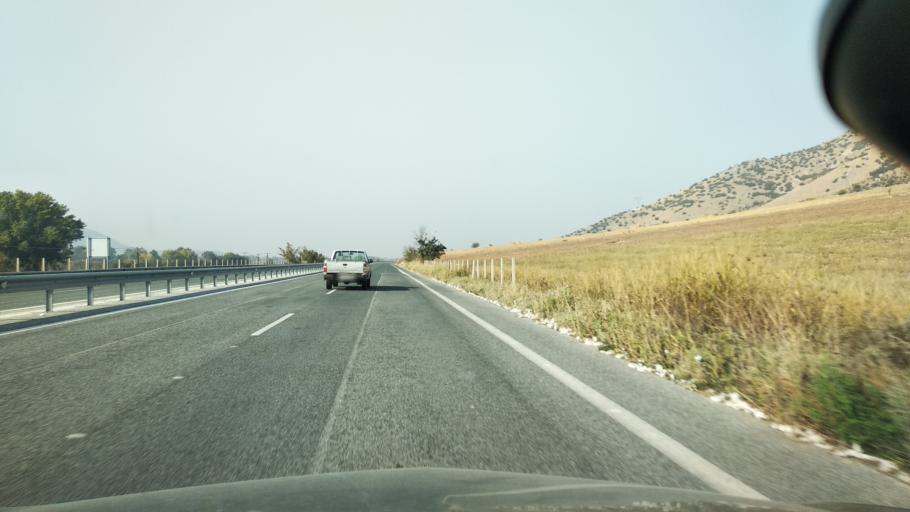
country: GR
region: Thessaly
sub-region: Trikala
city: Zarkos
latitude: 39.5882
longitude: 22.1550
